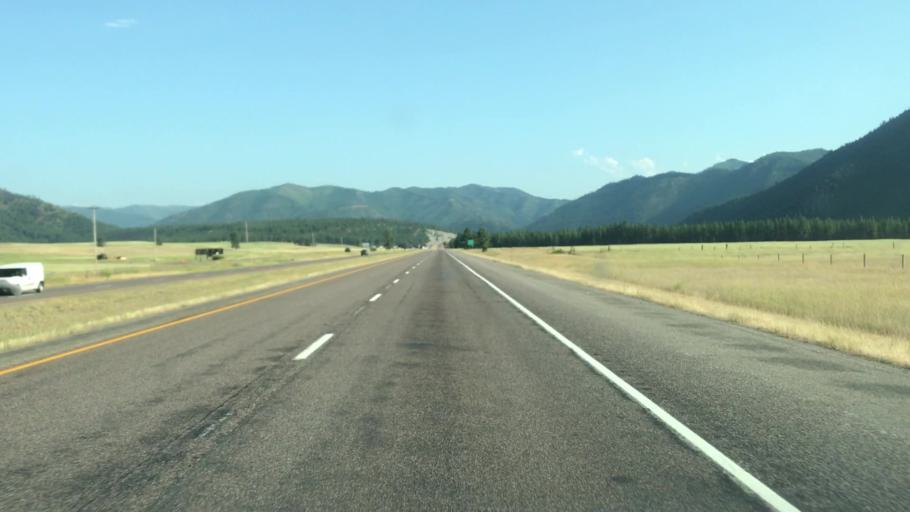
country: US
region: Montana
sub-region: Mineral County
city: Superior
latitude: 47.0455
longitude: -114.7526
